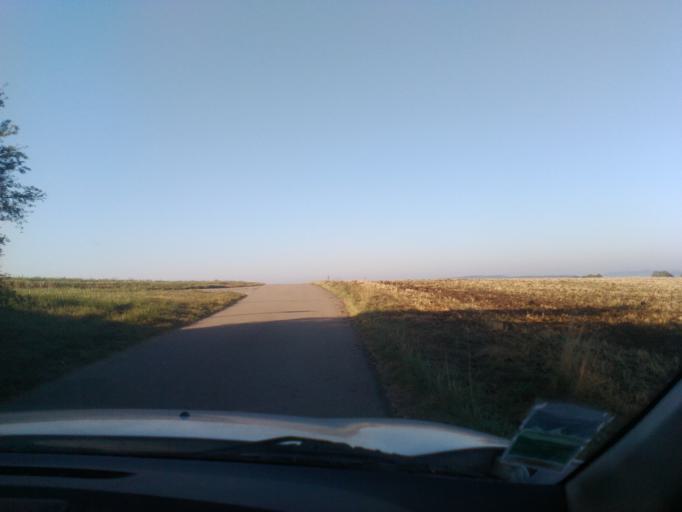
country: FR
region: Lorraine
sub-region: Departement des Vosges
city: Mirecourt
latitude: 48.2693
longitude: 6.1853
